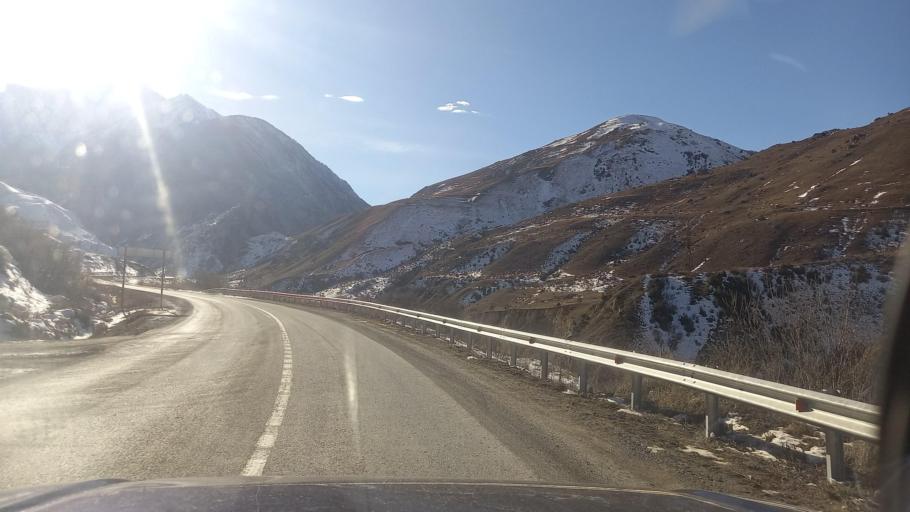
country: RU
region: North Ossetia
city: Chikola
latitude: 42.9965
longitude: 43.7845
